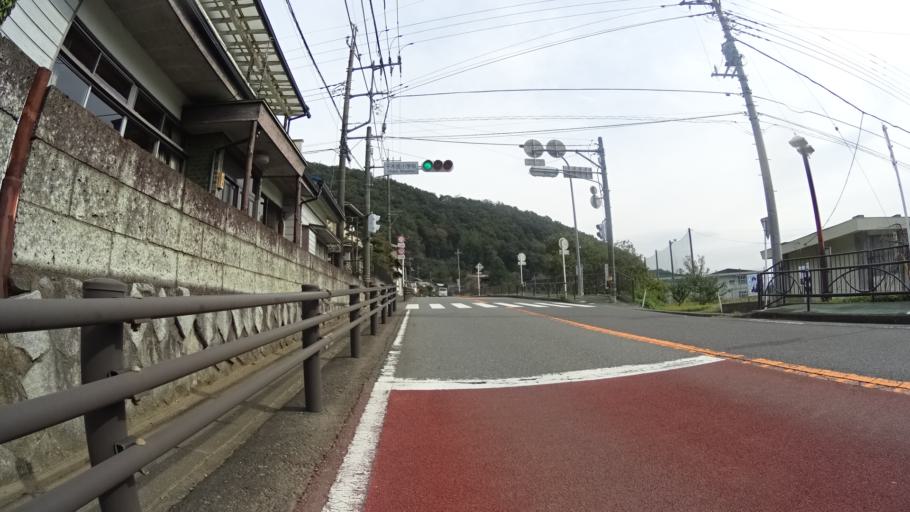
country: JP
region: Yamanashi
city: Uenohara
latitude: 35.6202
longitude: 139.2079
